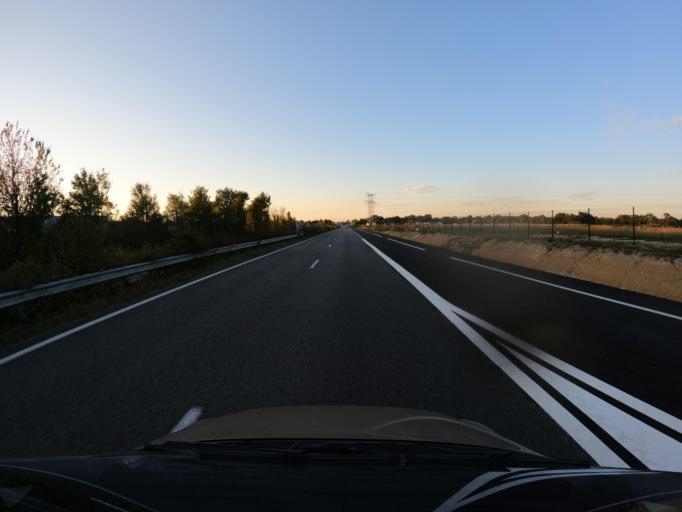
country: FR
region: Pays de la Loire
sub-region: Departement de la Vendee
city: Belleville-sur-Vie
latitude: 46.7901
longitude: -1.4243
